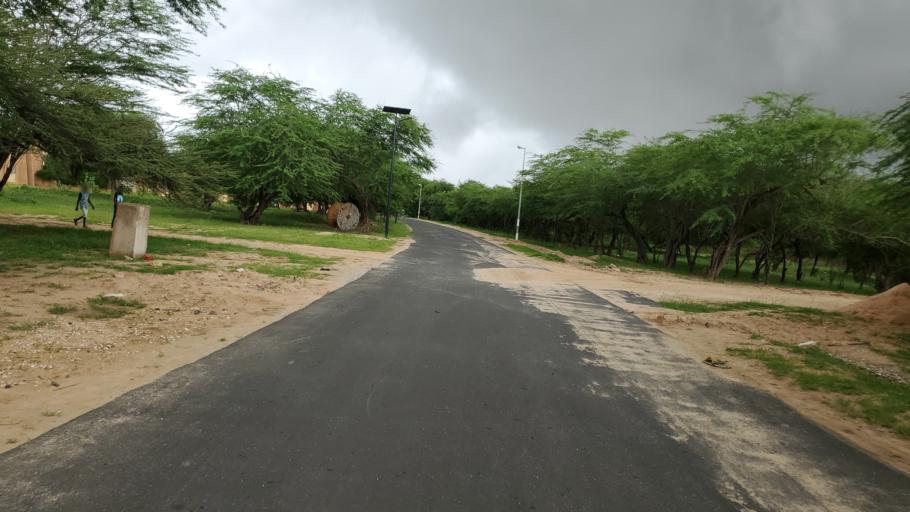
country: SN
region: Saint-Louis
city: Saint-Louis
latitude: 16.0639
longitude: -16.4281
